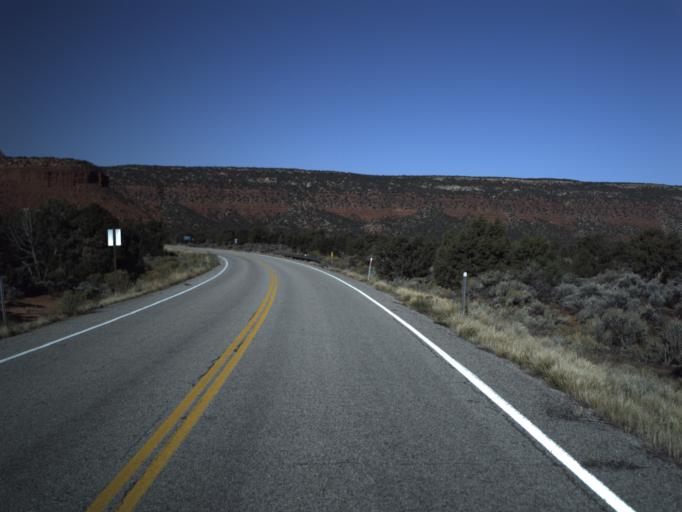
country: US
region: Utah
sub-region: San Juan County
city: Blanding
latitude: 37.5626
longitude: -110.0132
